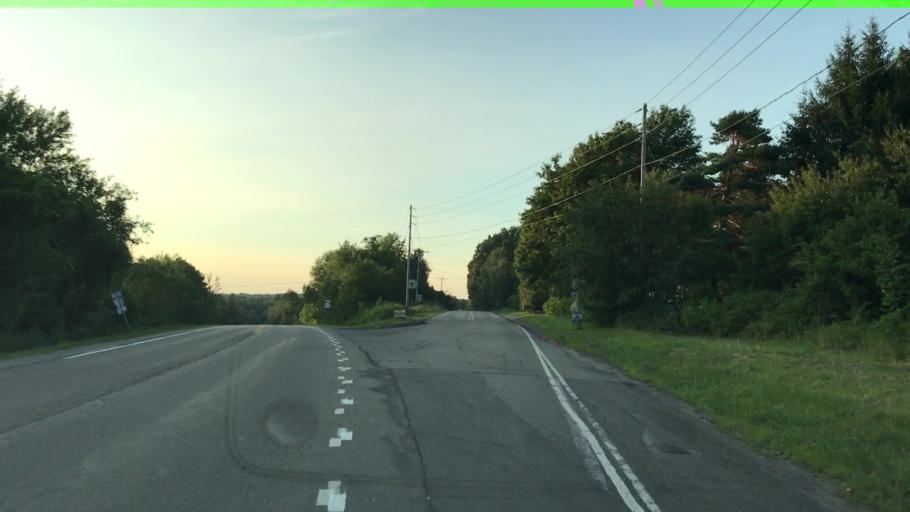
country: US
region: New York
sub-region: Chautauqua County
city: Mayville
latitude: 42.2584
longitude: -79.4686
